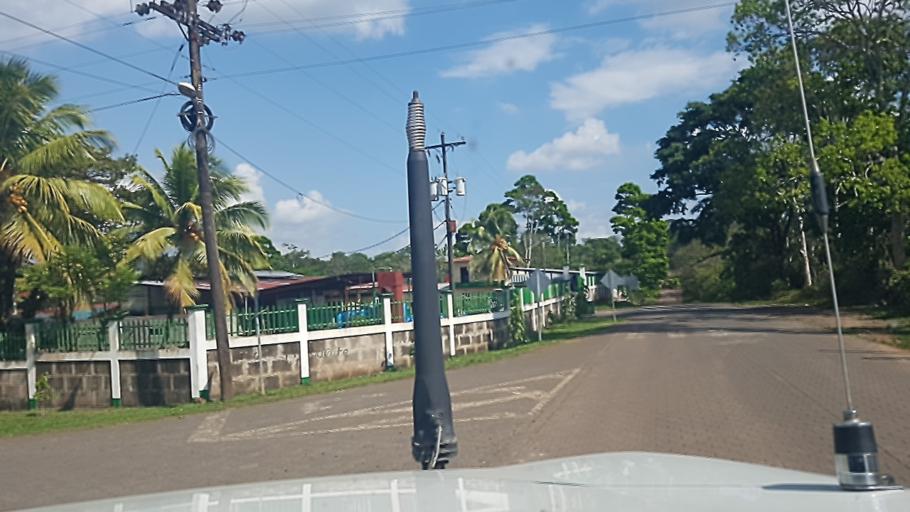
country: NI
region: Atlantico Sur
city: Nueva Guinea
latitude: 11.6791
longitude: -84.4495
